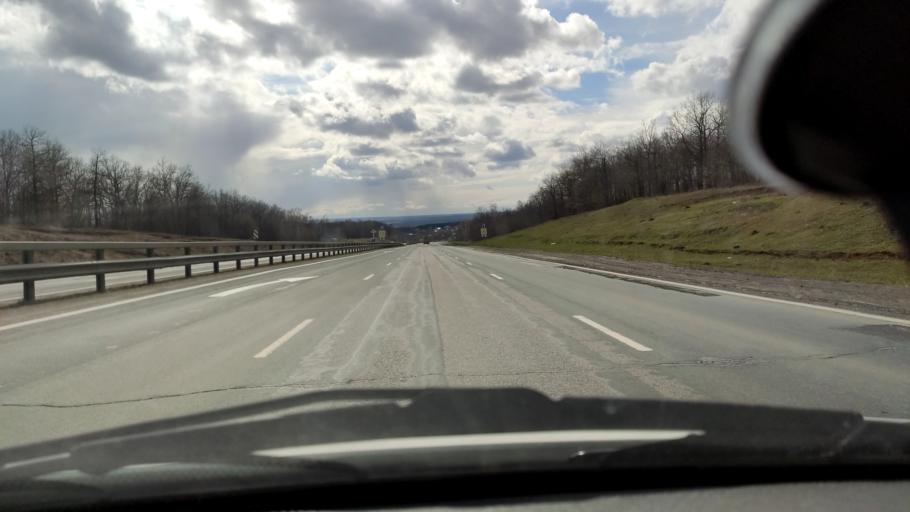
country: RU
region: Bashkortostan
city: Avdon
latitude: 54.6420
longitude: 55.6156
